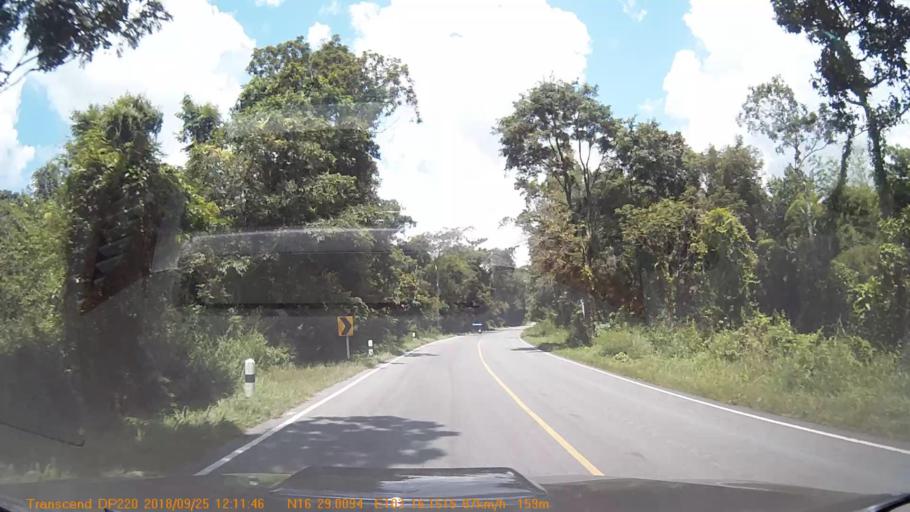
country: TH
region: Kalasin
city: Huai Mek
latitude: 16.4837
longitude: 103.2692
